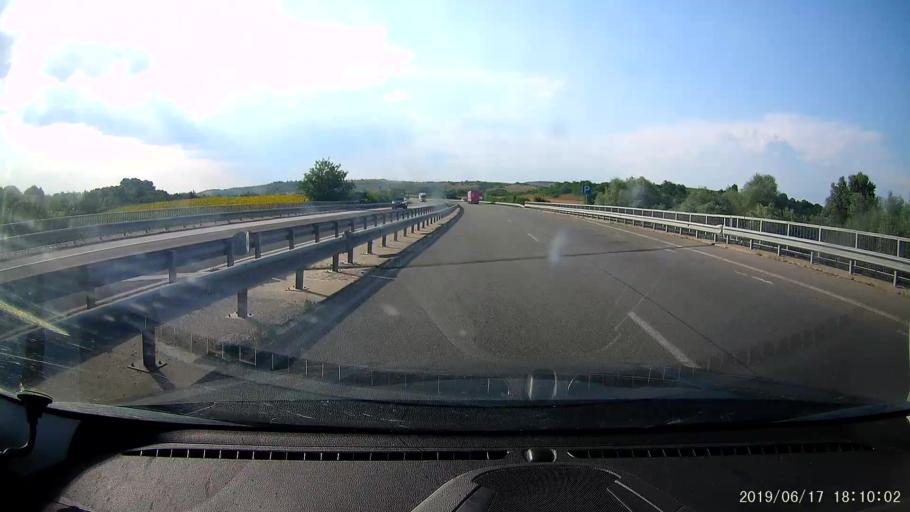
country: BG
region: Khaskovo
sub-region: Obshtina Lyubimets
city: Lyubimets
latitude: 41.8692
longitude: 26.0839
